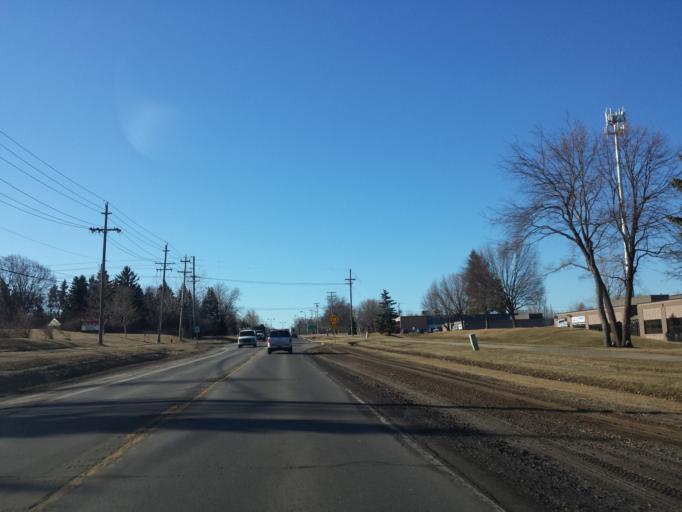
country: US
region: Michigan
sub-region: Oakland County
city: Rochester Hills
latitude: 42.6549
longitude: -83.1529
